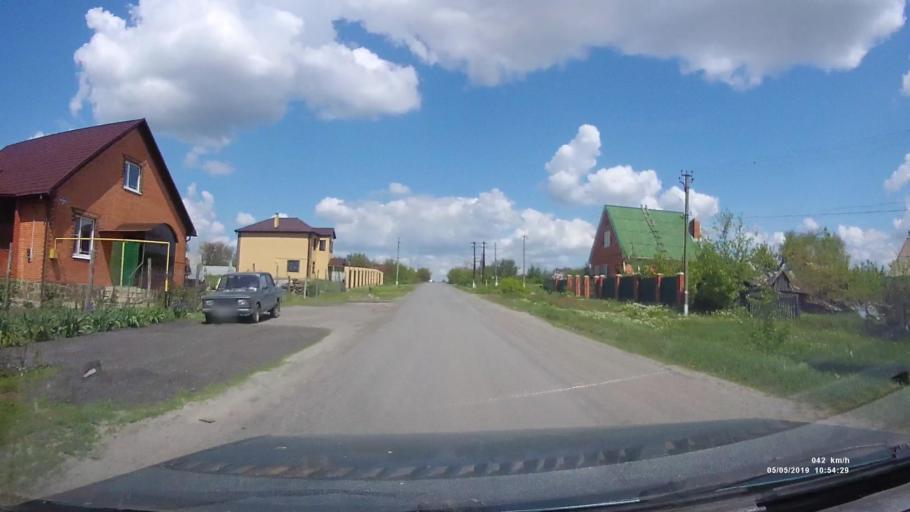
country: RU
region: Rostov
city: Ust'-Donetskiy
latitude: 47.6585
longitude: 40.8230
